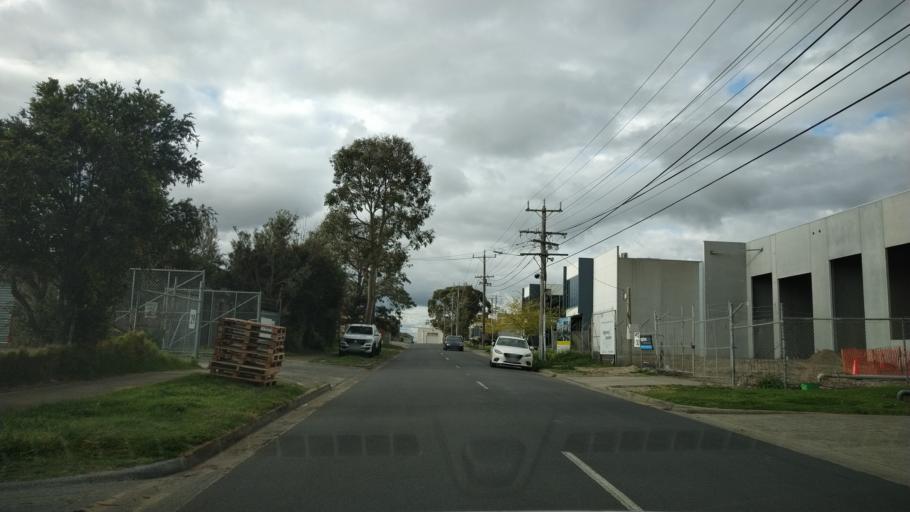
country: AU
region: Victoria
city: Highett
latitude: -37.9505
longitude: 145.0664
